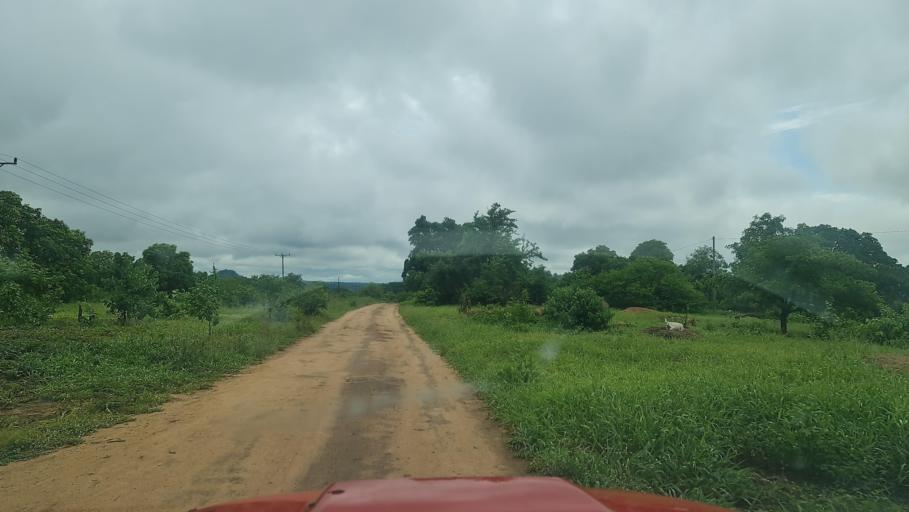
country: MW
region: Southern Region
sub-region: Nsanje District
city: Nsanje
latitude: -17.1809
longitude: 35.9084
